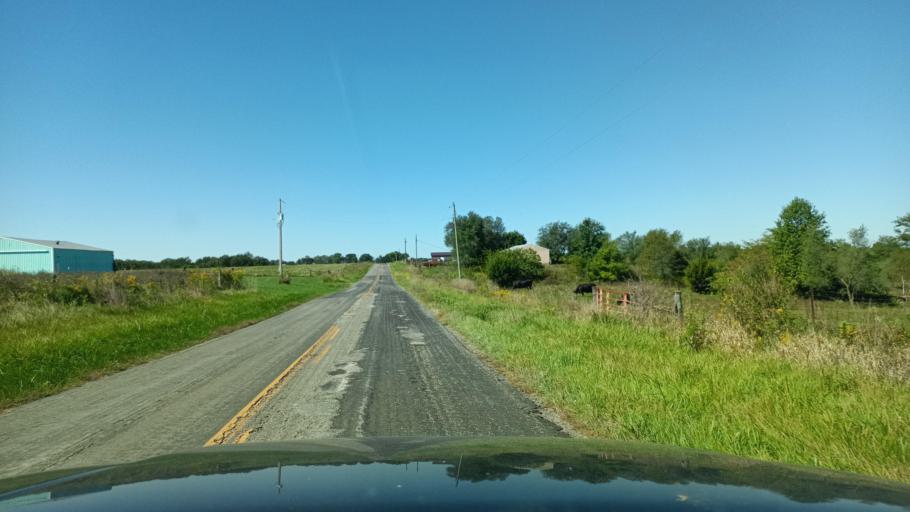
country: US
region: Missouri
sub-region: Scotland County
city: Memphis
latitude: 40.3543
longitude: -92.2855
